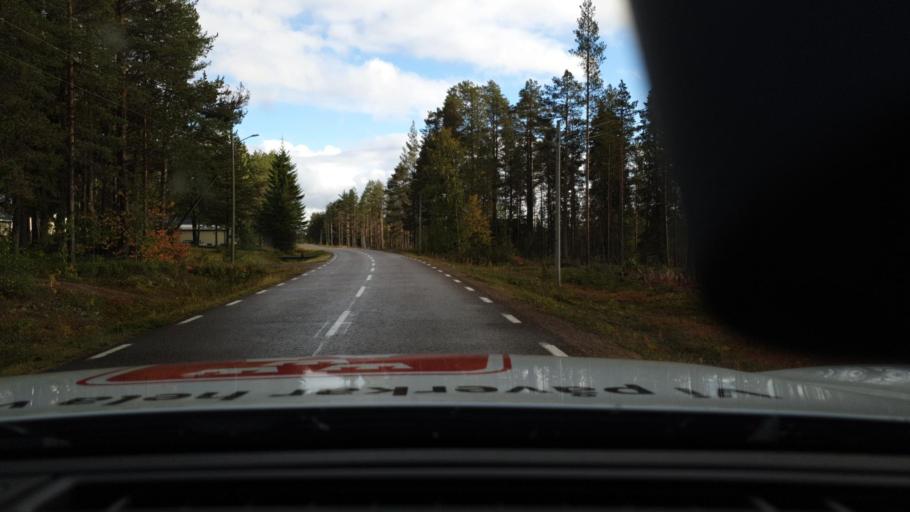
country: SE
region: Norrbotten
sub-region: Overkalix Kommun
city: OEverkalix
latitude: 67.0093
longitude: 22.4838
